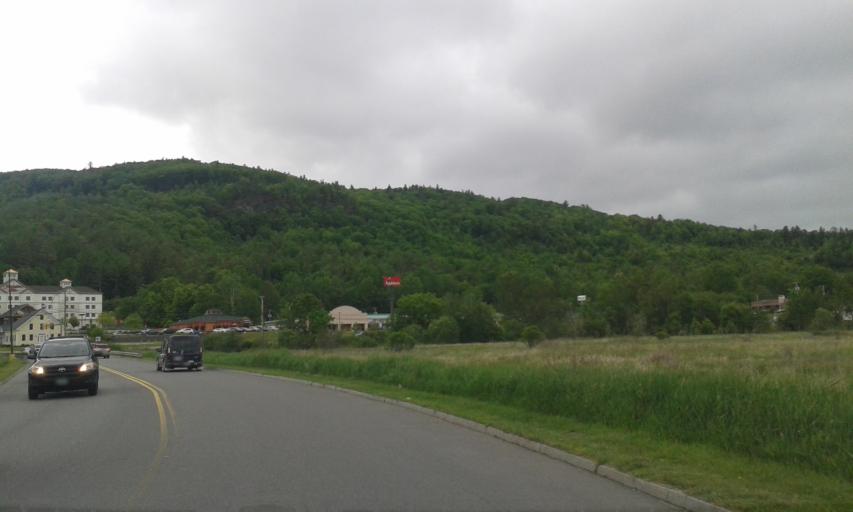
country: US
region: New Hampshire
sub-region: Grafton County
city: Littleton
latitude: 44.3045
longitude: -71.8014
